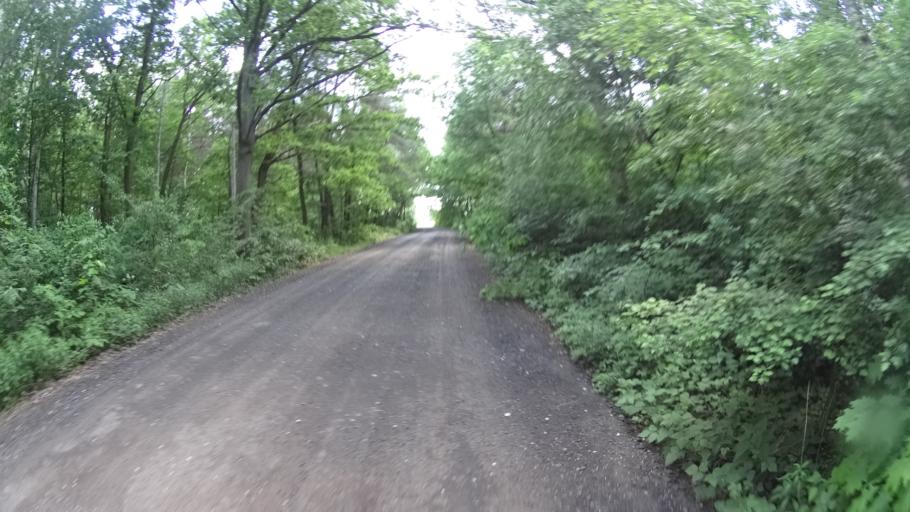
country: PL
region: Masovian Voivodeship
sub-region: Powiat pruszkowski
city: Nadarzyn
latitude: 52.0640
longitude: 20.8210
